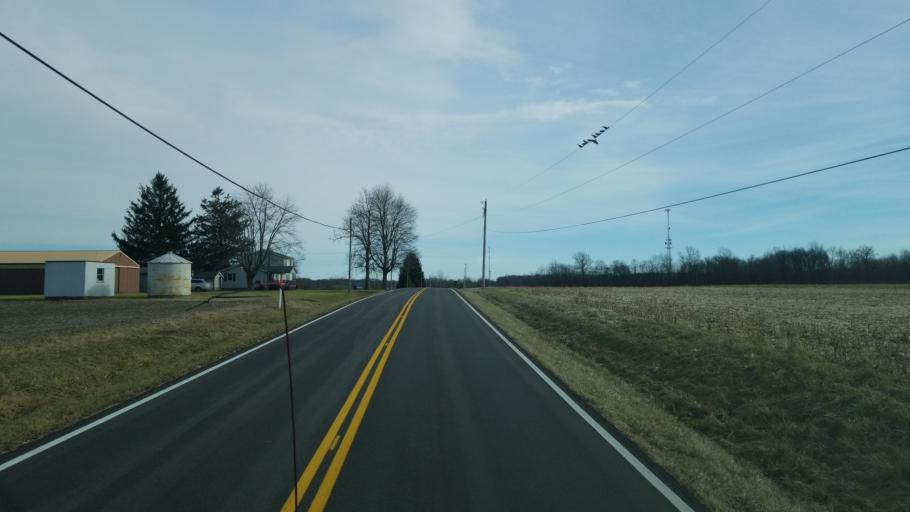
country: US
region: Ohio
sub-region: Warren County
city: Morrow
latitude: 39.4295
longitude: -84.0938
